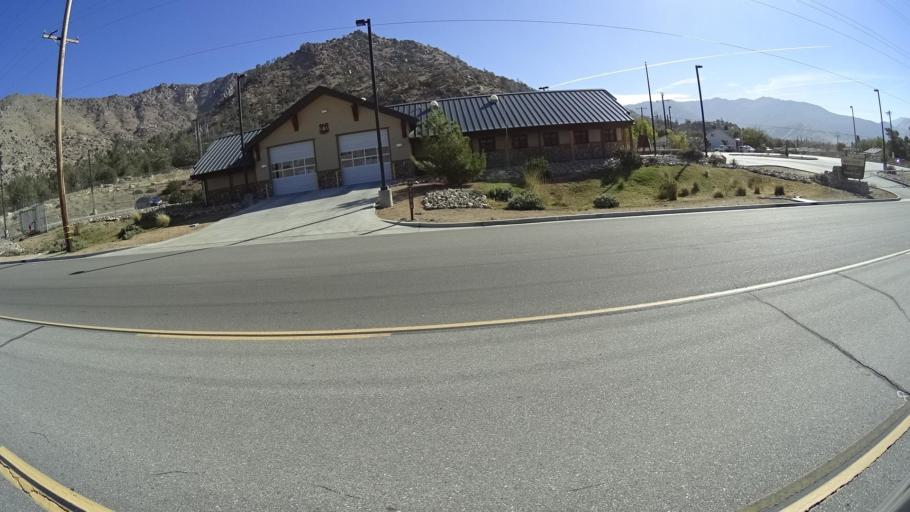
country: US
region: California
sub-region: Kern County
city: Lake Isabella
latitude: 35.6393
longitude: -118.4656
